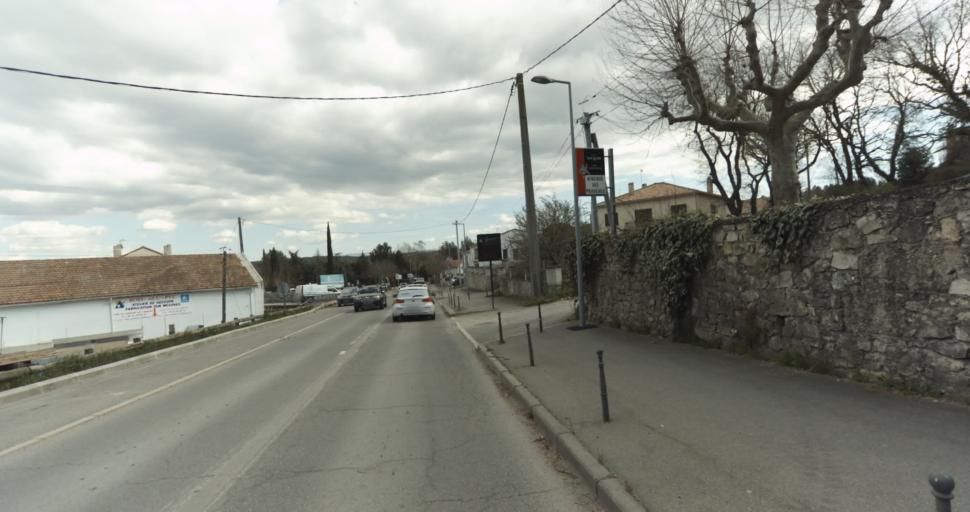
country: FR
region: Provence-Alpes-Cote d'Azur
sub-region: Departement des Bouches-du-Rhone
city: Greasque
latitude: 43.4342
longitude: 5.5395
